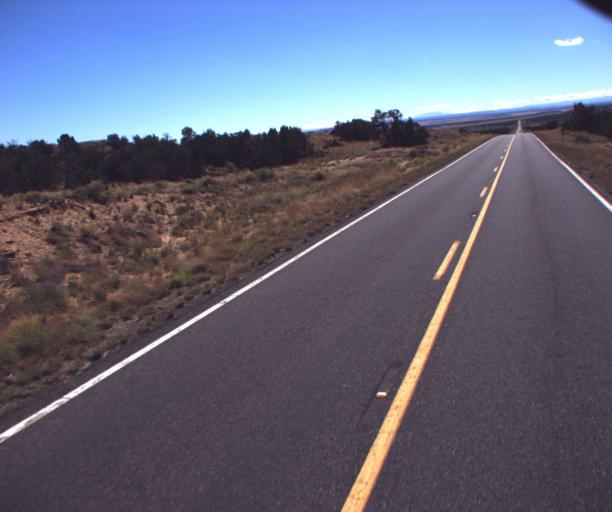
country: US
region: Arizona
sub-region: Apache County
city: Saint Johns
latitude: 34.8185
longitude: -109.2376
